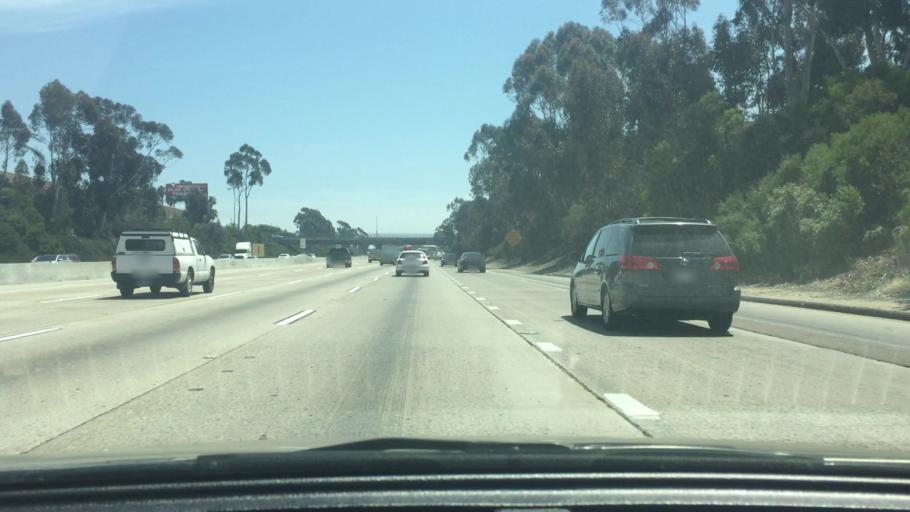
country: US
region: California
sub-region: San Diego County
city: National City
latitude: 32.7002
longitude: -117.0950
